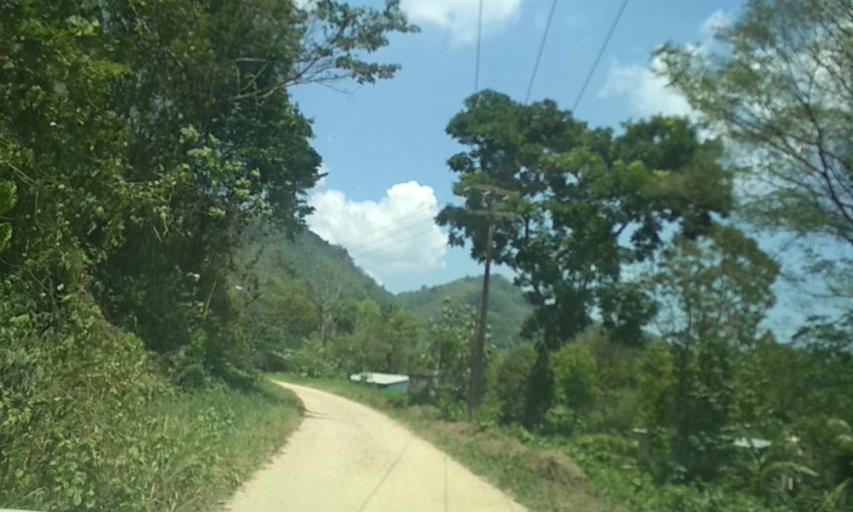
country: MX
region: Chiapas
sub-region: Tecpatan
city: Raudales Malpaso
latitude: 17.2806
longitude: -93.8298
